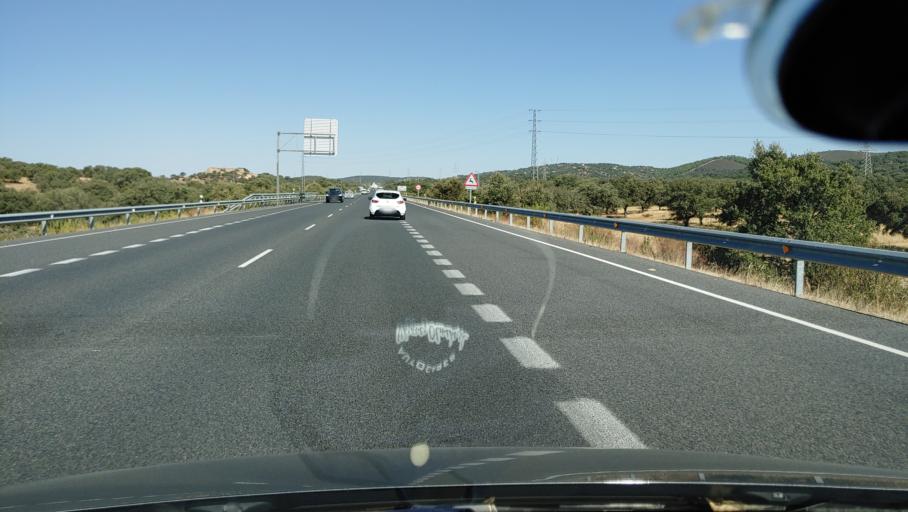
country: ES
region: Andalusia
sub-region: Province of Cordoba
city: Obejo
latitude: 38.0787
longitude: -4.8489
